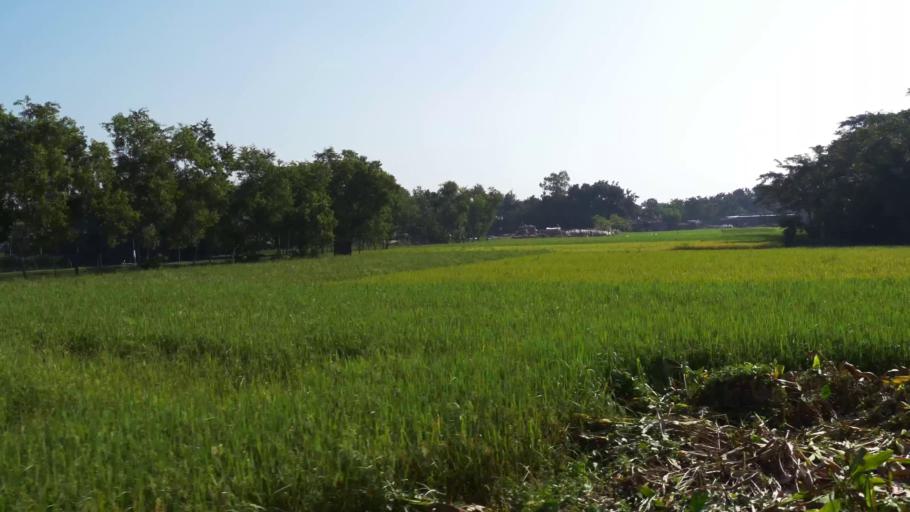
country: BD
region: Dhaka
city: Muktagacha
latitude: 24.8121
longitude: 90.2920
